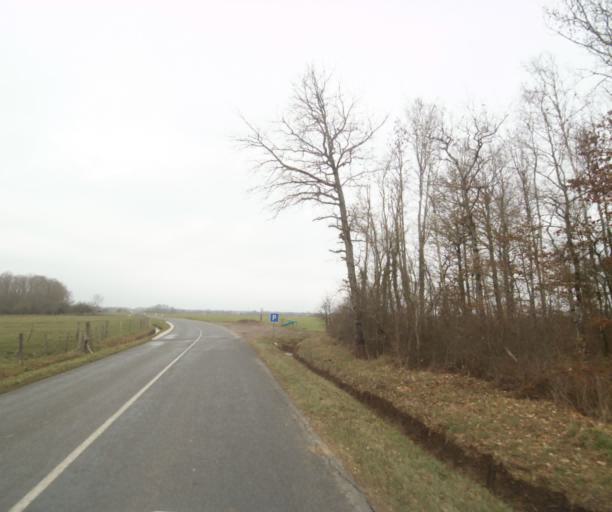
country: FR
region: Champagne-Ardenne
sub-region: Departement de la Marne
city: Pargny-sur-Saulx
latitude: 48.7365
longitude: 4.8602
